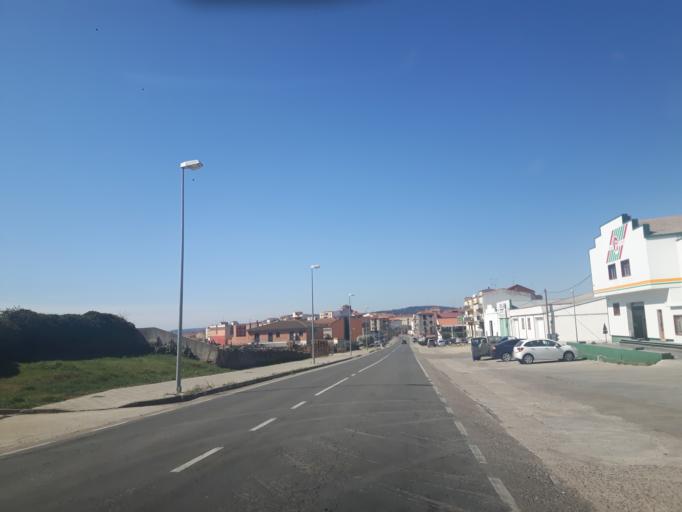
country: ES
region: Castille and Leon
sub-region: Provincia de Salamanca
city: Alba de Tormes
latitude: 40.8280
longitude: -5.5046
